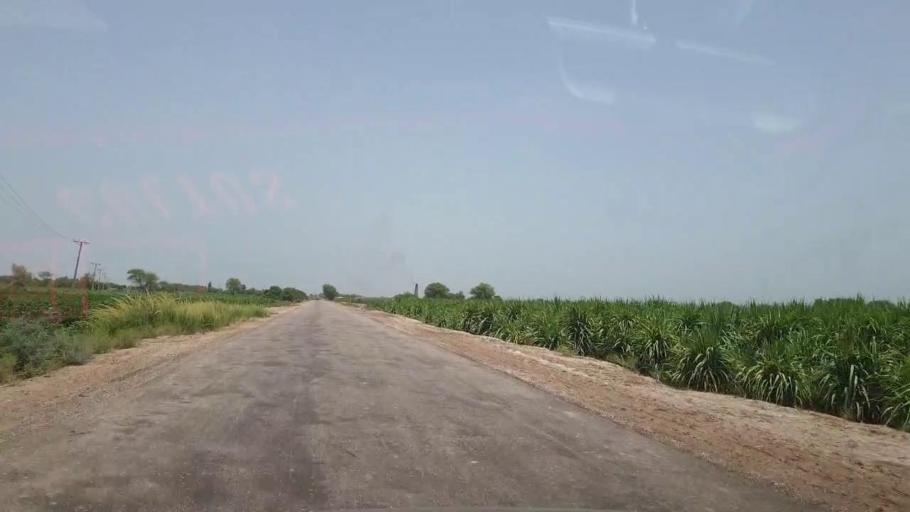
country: PK
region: Sindh
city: Daulatpur
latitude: 26.3893
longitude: 68.0841
